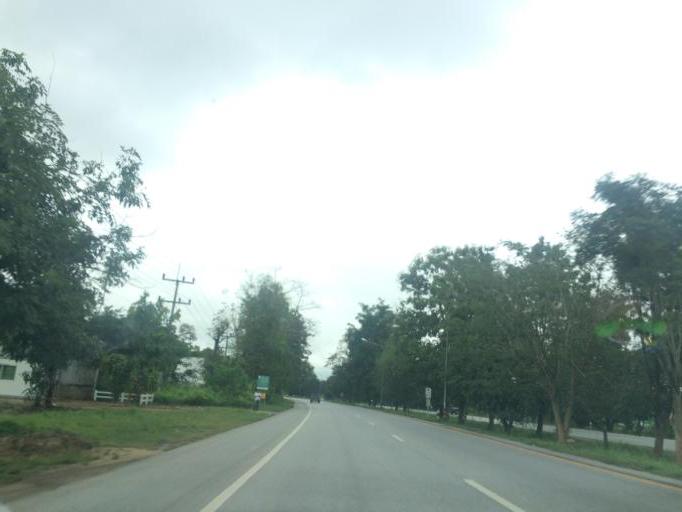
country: TH
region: Chiang Rai
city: Mae Lao
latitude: 19.7604
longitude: 99.7343
